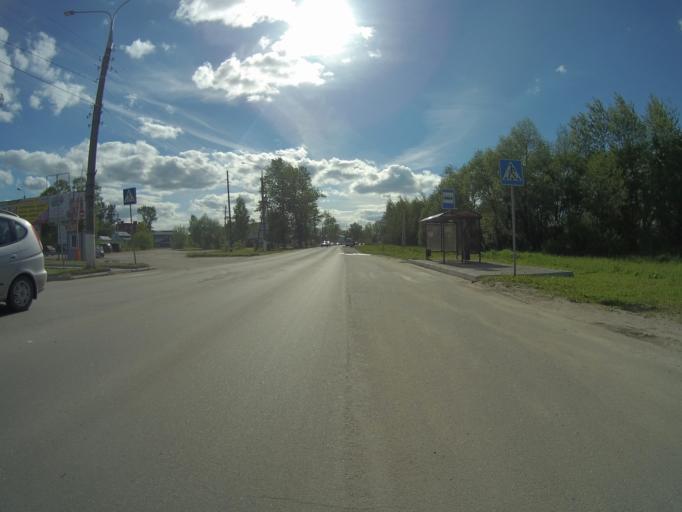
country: RU
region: Vladimir
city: Sudogda
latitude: 55.9519
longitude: 40.8753
